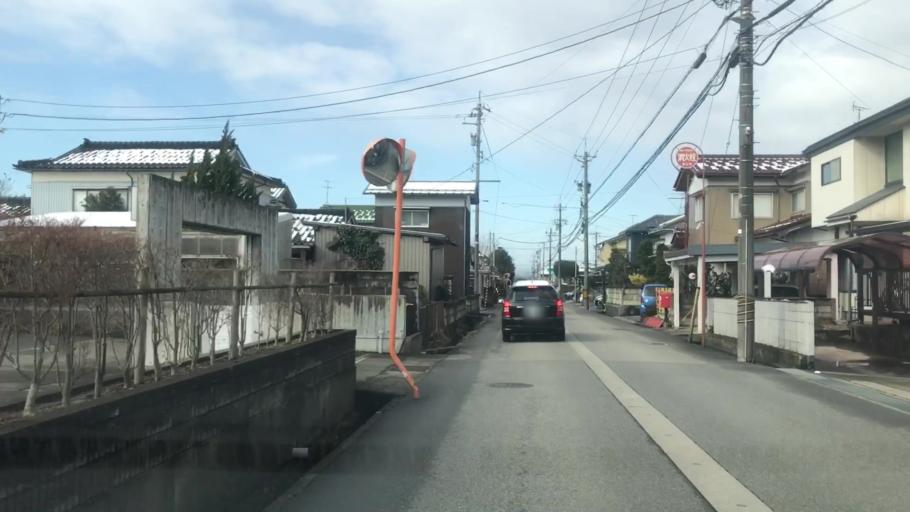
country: JP
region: Toyama
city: Toyama-shi
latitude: 36.6504
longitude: 137.2235
